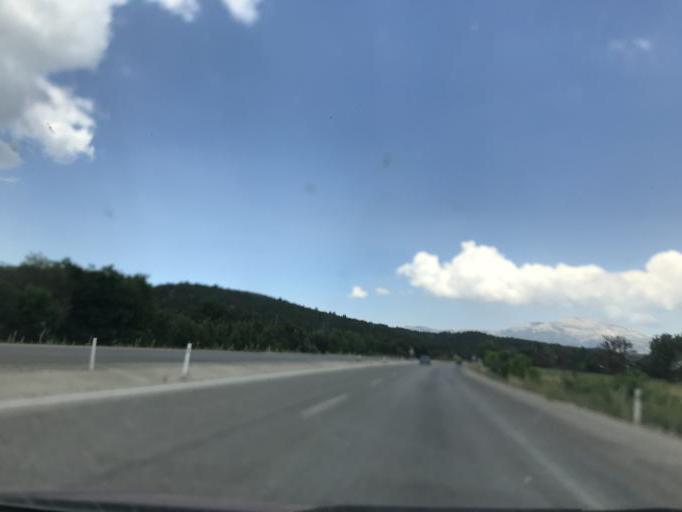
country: TR
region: Denizli
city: Tavas
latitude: 37.6093
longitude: 29.1359
